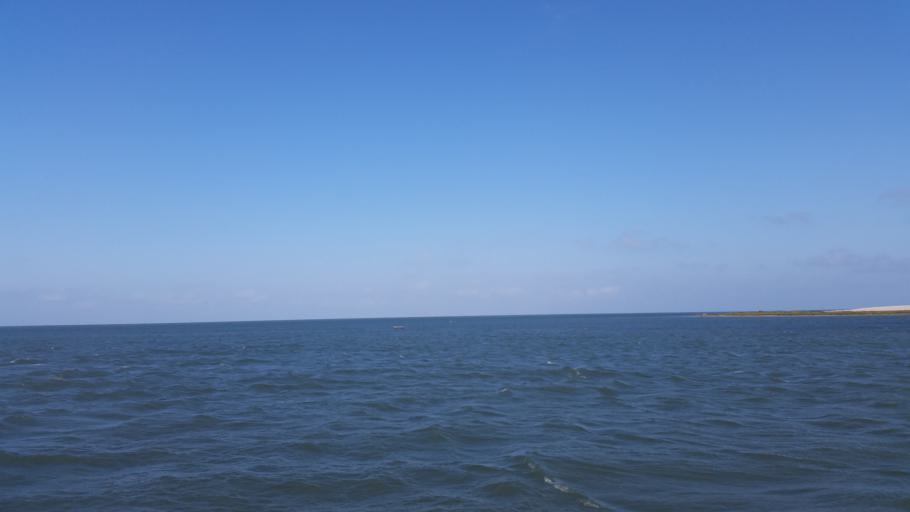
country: US
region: North Carolina
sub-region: Dare County
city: Buxton
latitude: 35.2125
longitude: -75.7156
